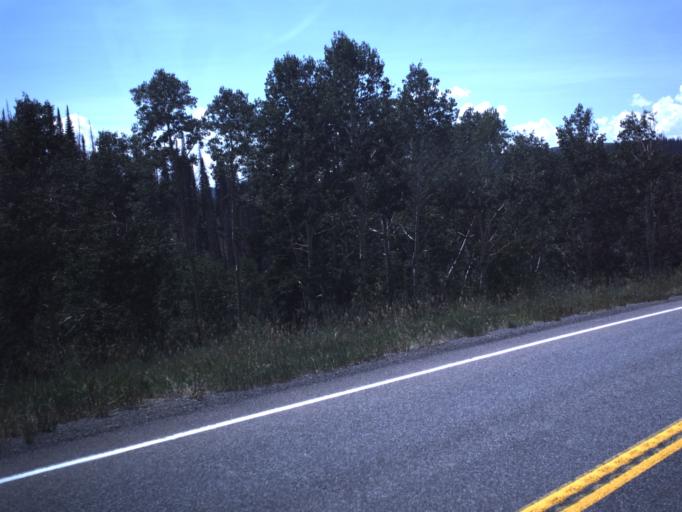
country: US
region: Utah
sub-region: Sanpete County
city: Fairview
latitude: 39.6830
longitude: -111.2321
